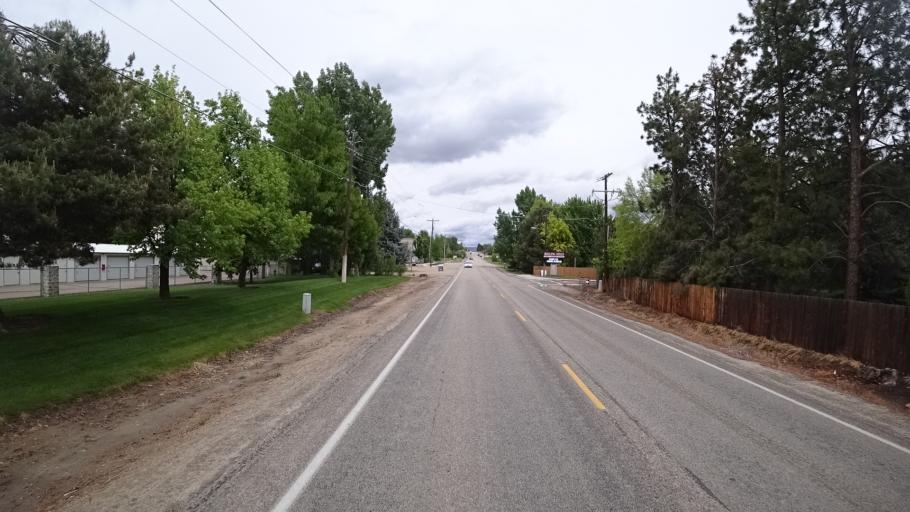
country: US
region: Idaho
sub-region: Ada County
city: Eagle
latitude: 43.6889
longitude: -116.3140
